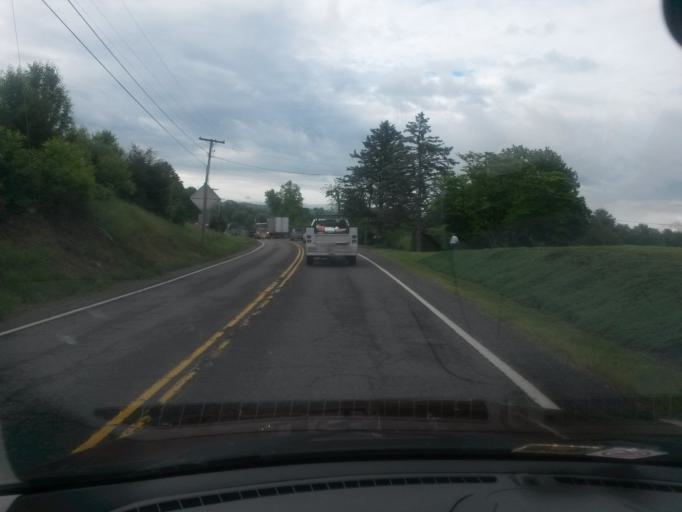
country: US
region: Virginia
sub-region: Montgomery County
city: Christiansburg
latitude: 37.0773
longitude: -80.4522
